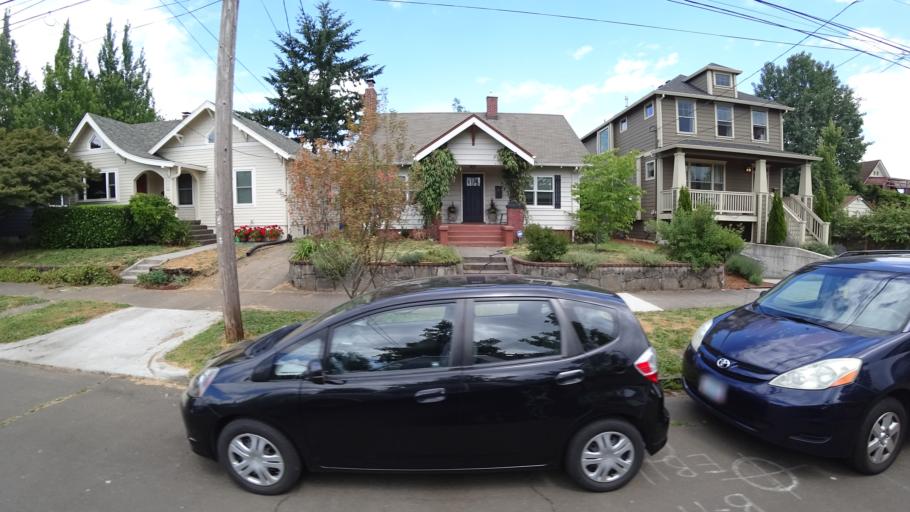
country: US
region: Oregon
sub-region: Washington County
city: West Haven
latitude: 45.5822
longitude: -122.7390
